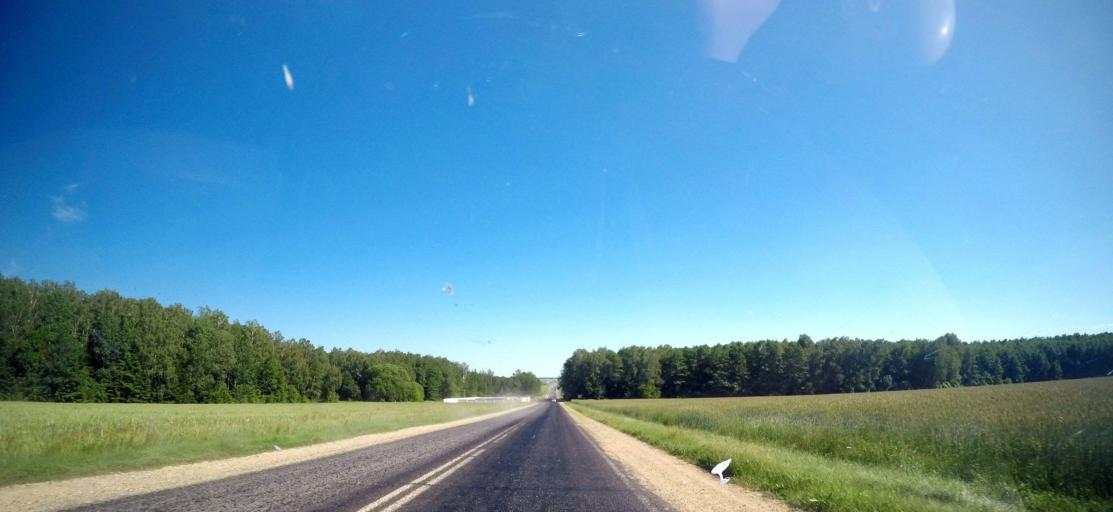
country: BY
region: Grodnenskaya
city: Vyalikaya Byerastavitsa
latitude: 53.2210
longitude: 23.9961
